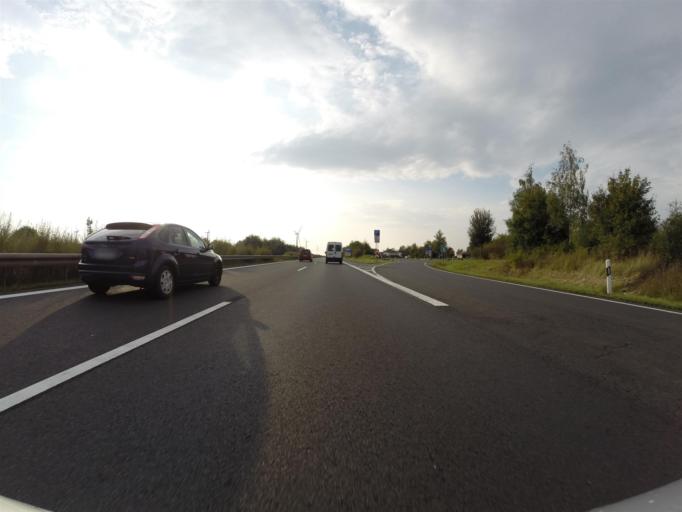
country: DE
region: Saxony-Anhalt
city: Grosskorbetha
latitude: 51.2560
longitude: 12.0033
